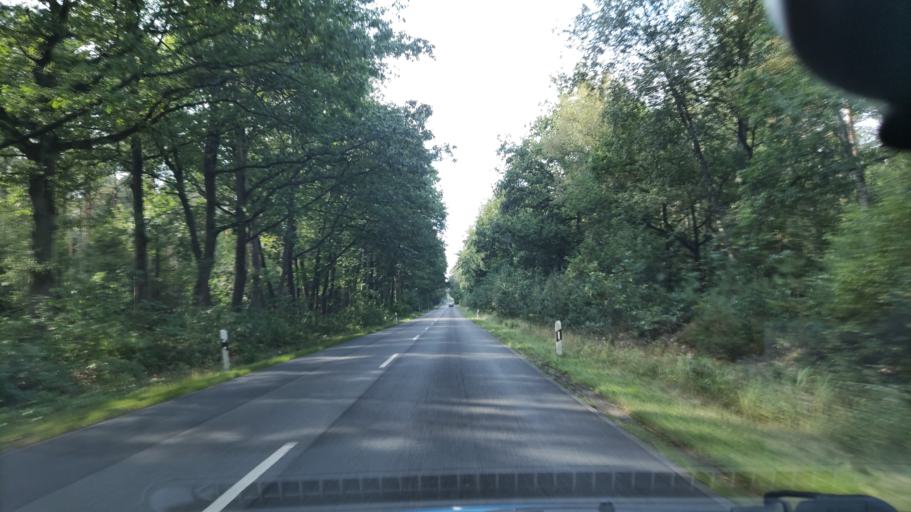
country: DE
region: Lower Saxony
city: Fassberg
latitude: 52.9694
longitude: 10.1591
